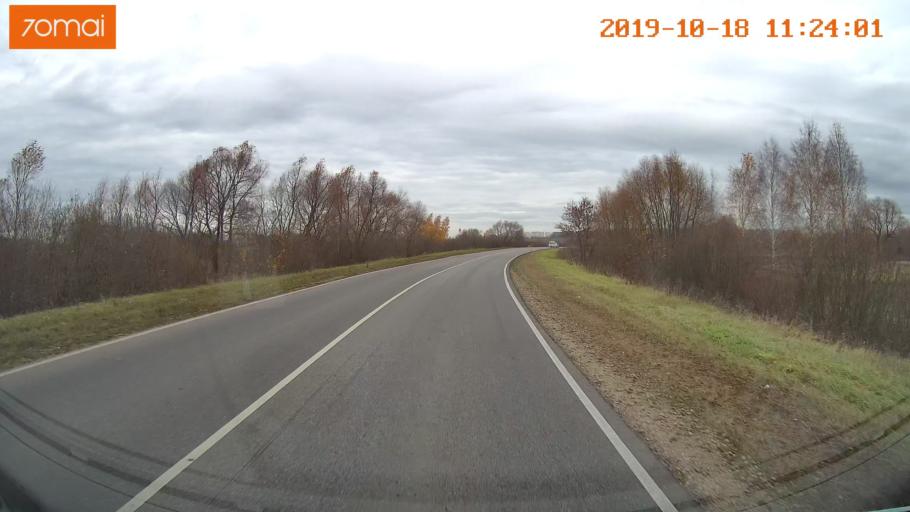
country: RU
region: Tula
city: Kimovsk
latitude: 54.1101
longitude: 38.5954
